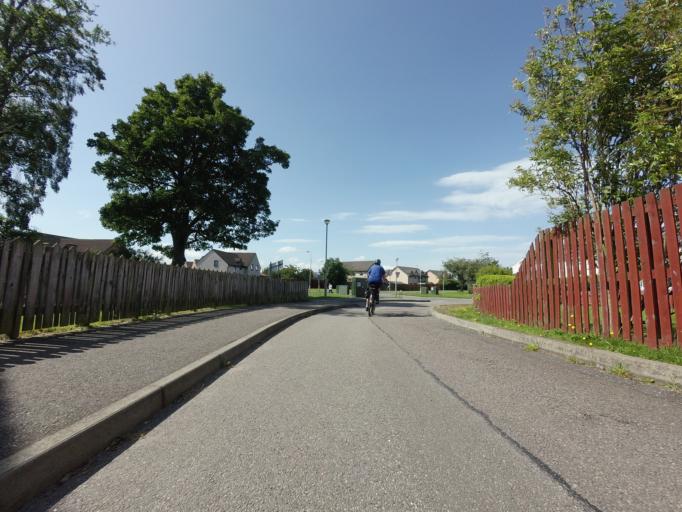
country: GB
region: Scotland
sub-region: Highland
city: Inverness
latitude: 57.4831
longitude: -4.1485
